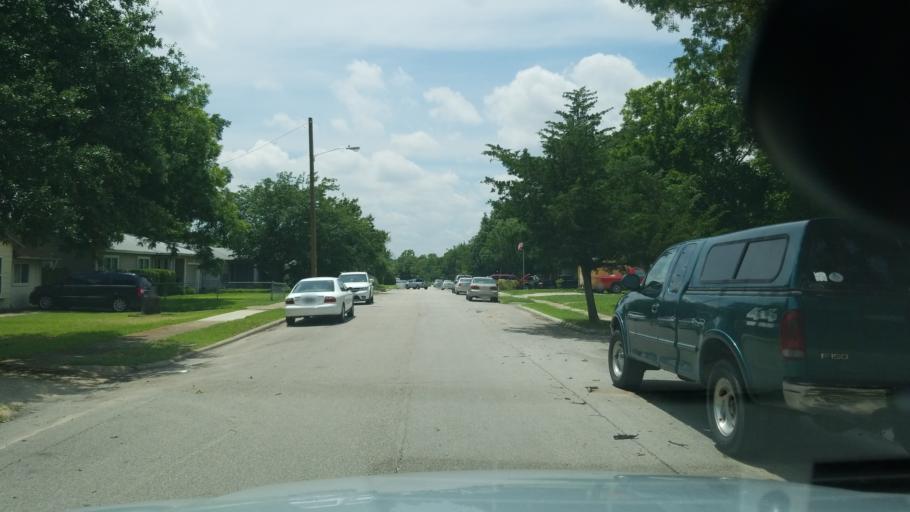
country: US
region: Texas
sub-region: Dallas County
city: Irving
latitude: 32.8433
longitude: -96.9740
